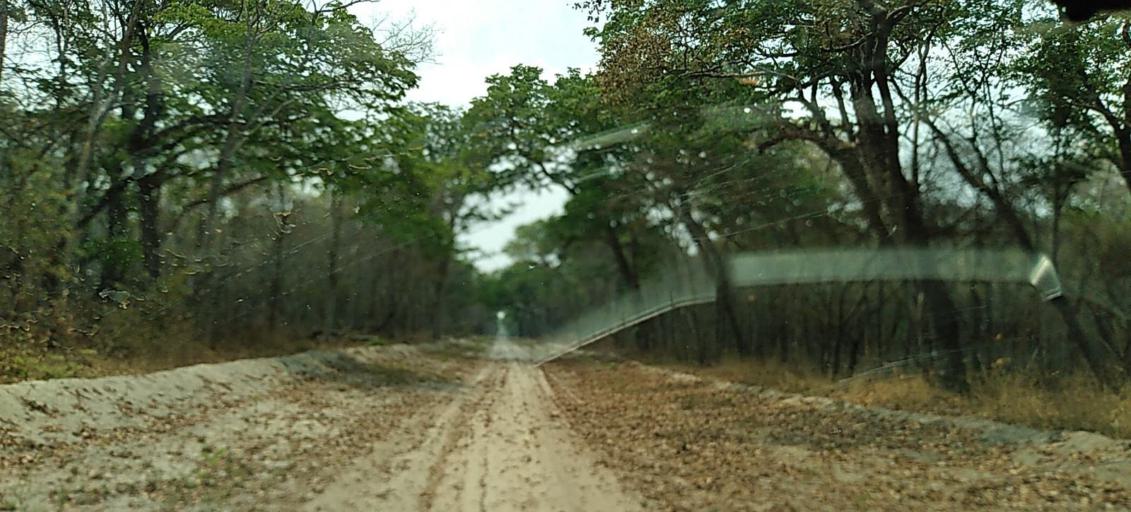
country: ZM
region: Western
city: Lukulu
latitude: -14.0151
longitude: 23.5802
